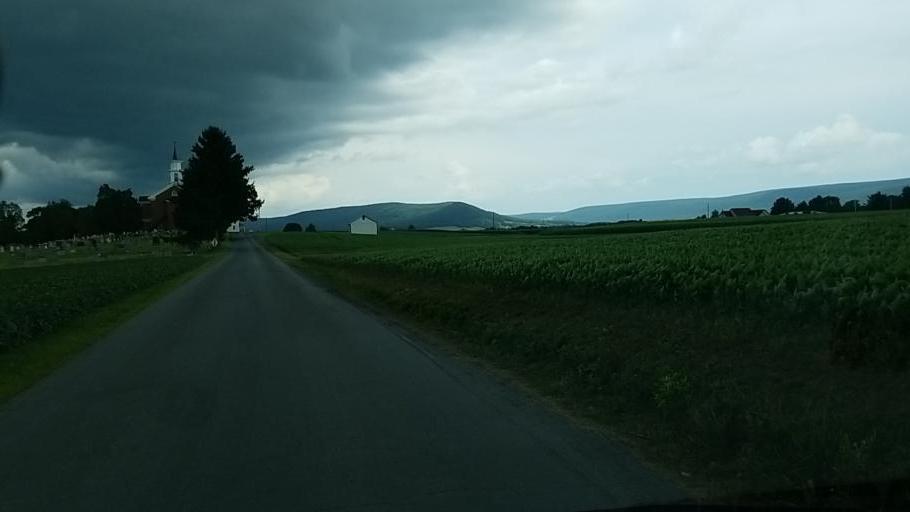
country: US
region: Pennsylvania
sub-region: Dauphin County
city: Elizabethville
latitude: 40.5868
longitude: -76.8201
